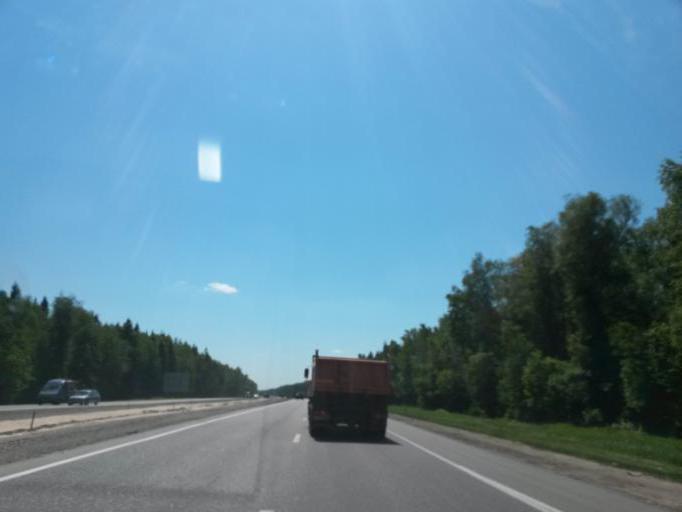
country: RU
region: Moskovskaya
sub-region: Chekhovskiy Rayon
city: Chekhov
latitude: 55.1804
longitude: 37.5356
